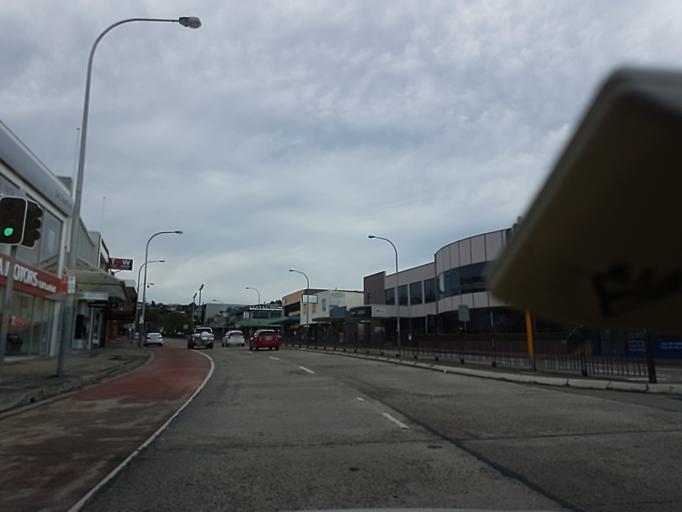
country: AU
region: New South Wales
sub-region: Warringah
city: Brookvale
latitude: -33.7641
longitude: 151.2713
